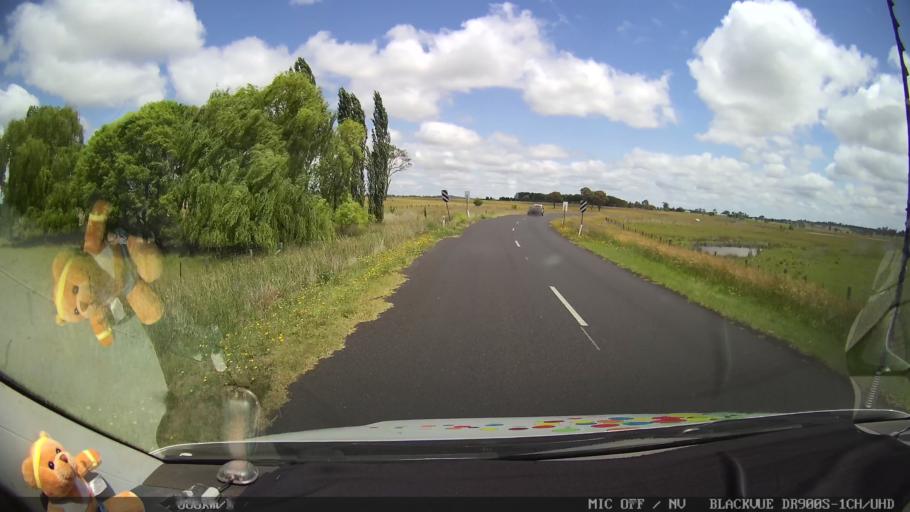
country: AU
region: New South Wales
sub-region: Glen Innes Severn
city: Glen Innes
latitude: -29.6820
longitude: 151.6994
